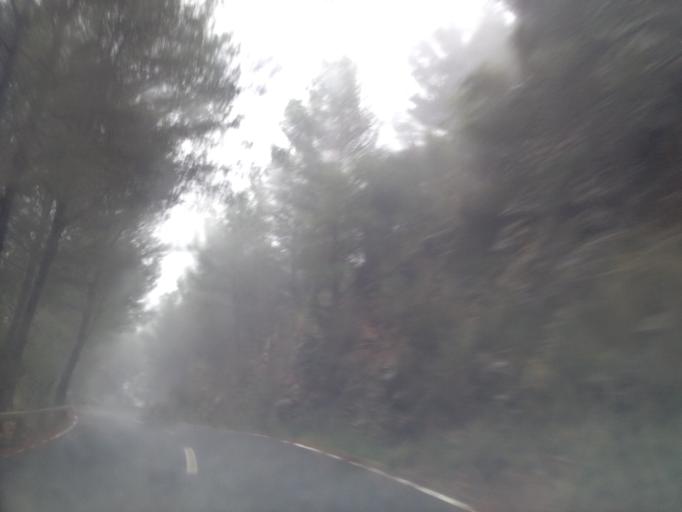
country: ES
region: Balearic Islands
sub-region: Illes Balears
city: Fornalutx
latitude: 39.7912
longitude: 2.7315
